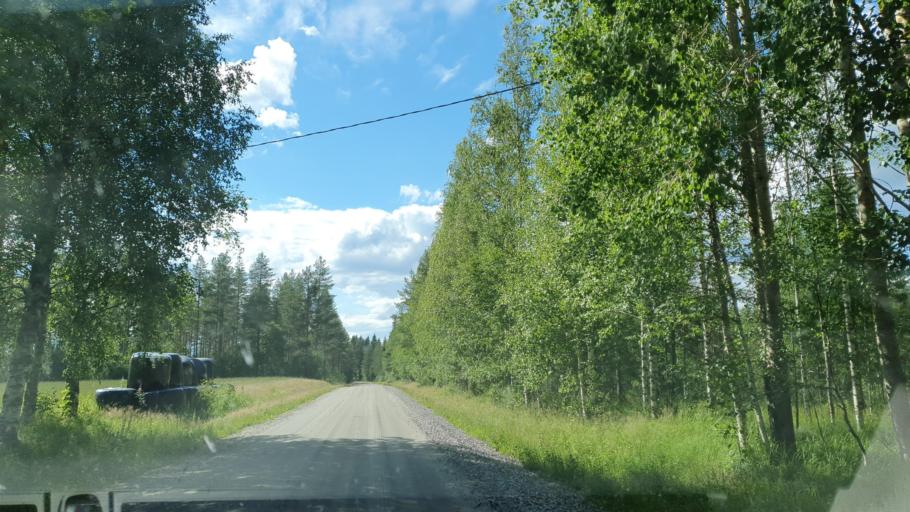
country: FI
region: Kainuu
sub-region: Kehys-Kainuu
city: Kuhmo
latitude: 64.1508
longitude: 29.7406
